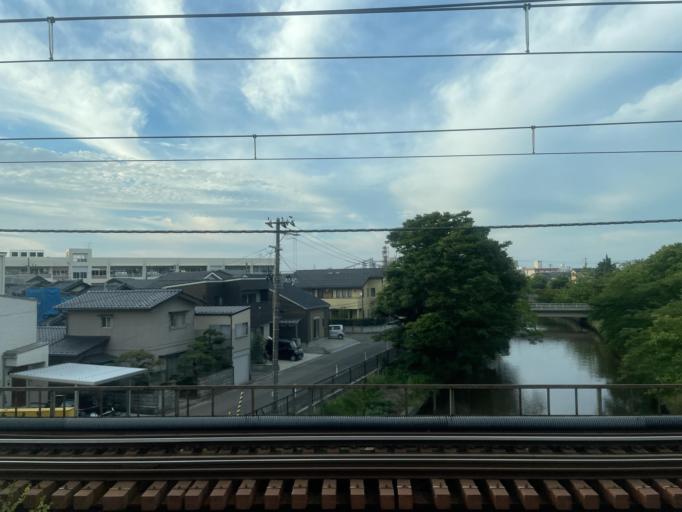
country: JP
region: Niigata
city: Niigata-shi
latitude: 37.9148
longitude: 139.0753
